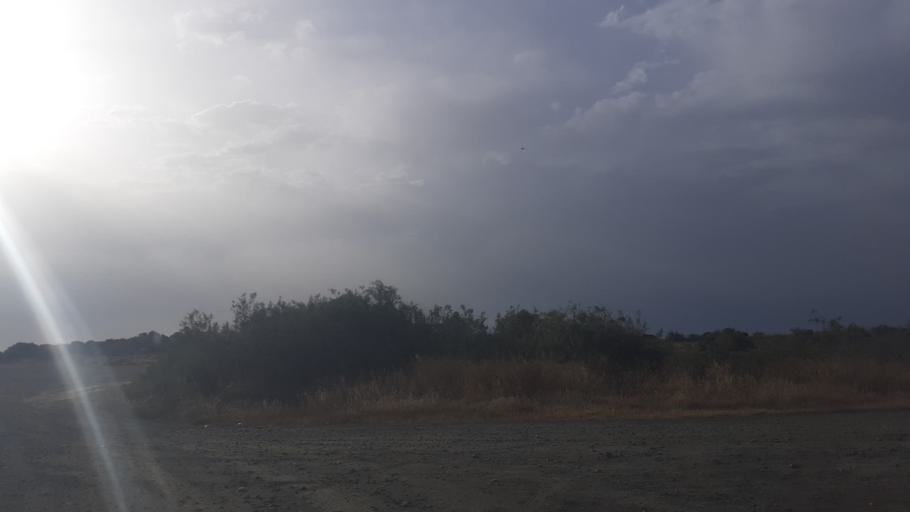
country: CY
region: Limassol
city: Limassol
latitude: 34.6440
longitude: 33.0090
